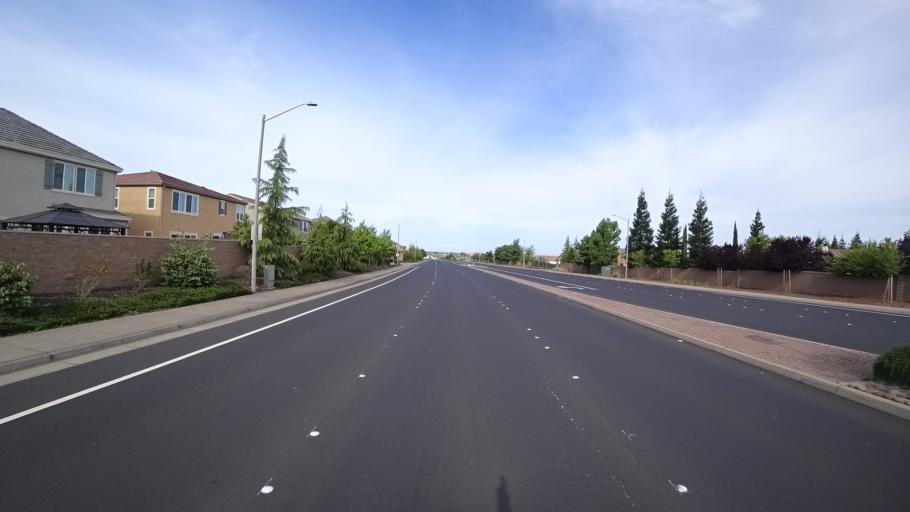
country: US
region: California
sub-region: Placer County
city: Rocklin
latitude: 38.8188
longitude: -121.2765
